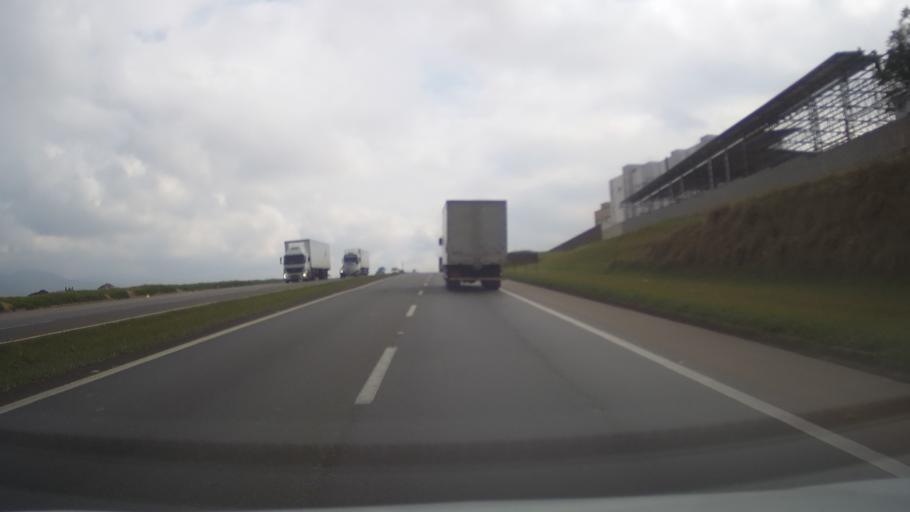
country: BR
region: Minas Gerais
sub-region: Extrema
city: Extrema
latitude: -22.8434
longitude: -46.3306
